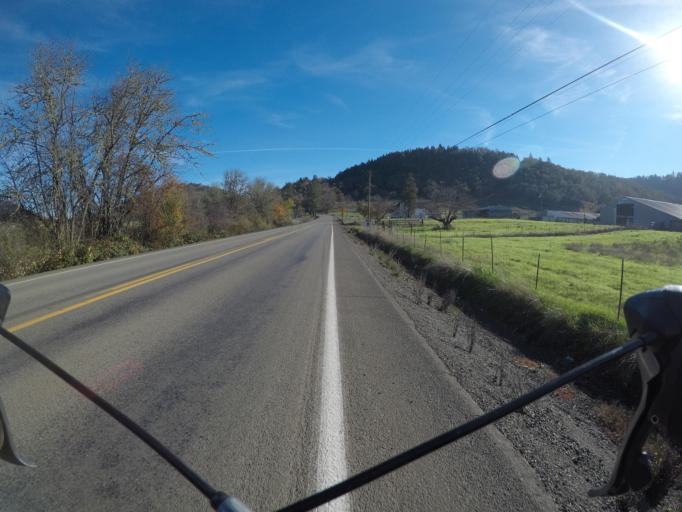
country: US
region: Oregon
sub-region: Douglas County
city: Winston
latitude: 43.1860
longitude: -123.4631
